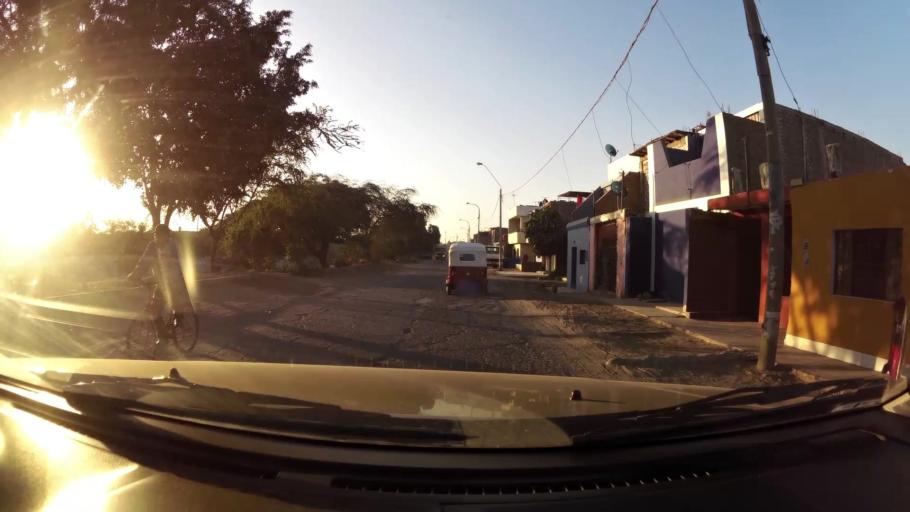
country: PE
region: Ica
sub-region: Provincia de Ica
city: Ica
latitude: -14.0739
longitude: -75.7194
